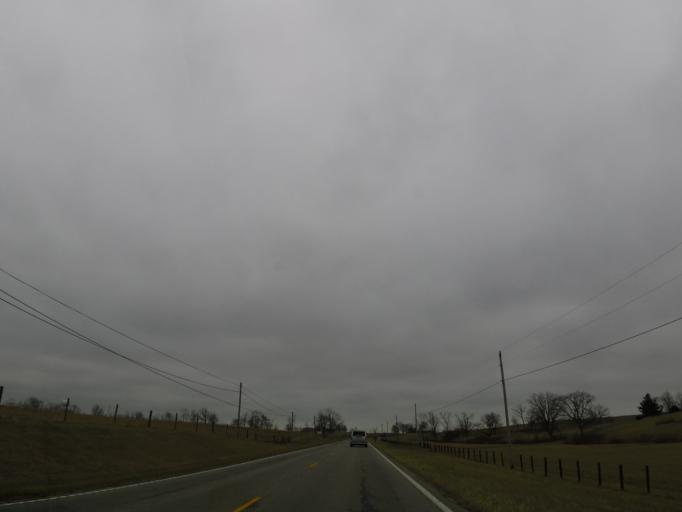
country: US
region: Kentucky
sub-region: Henry County
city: New Castle
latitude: 38.4742
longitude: -85.1716
